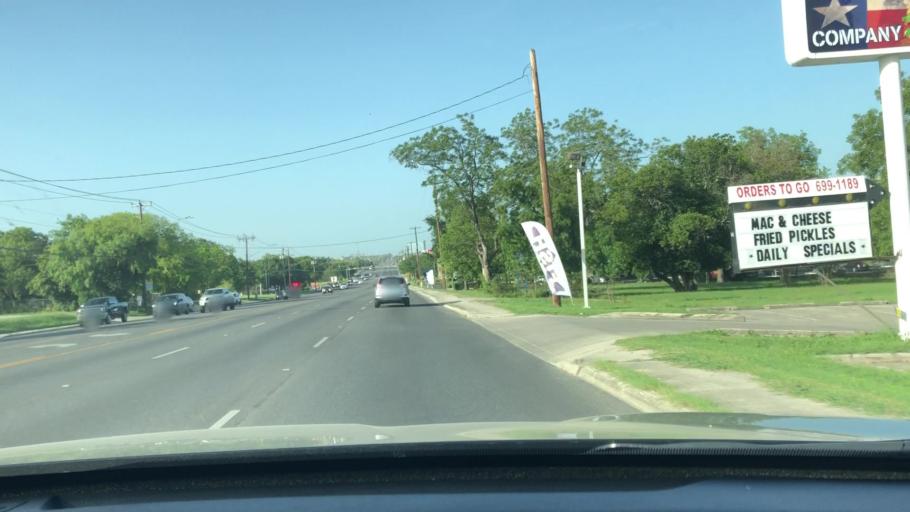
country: US
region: Texas
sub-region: Bexar County
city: Leon Valley
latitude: 29.5265
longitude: -98.5970
